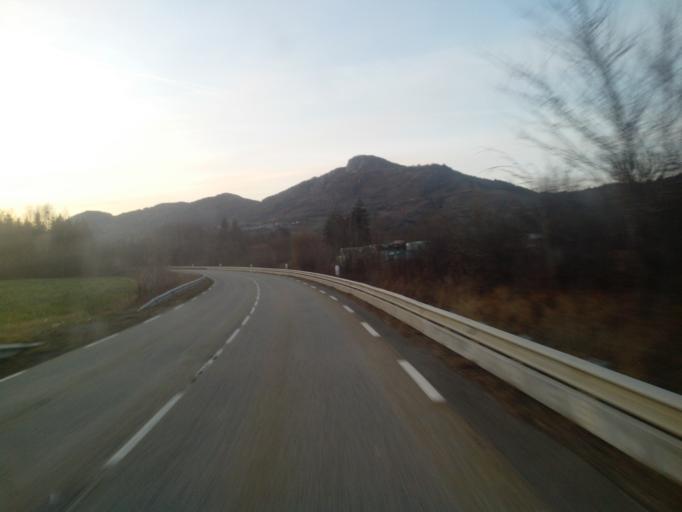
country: FR
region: Midi-Pyrenees
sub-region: Departement de l'Ariege
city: Saint-Paul-de-Jarrat
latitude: 42.9318
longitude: 1.7317
